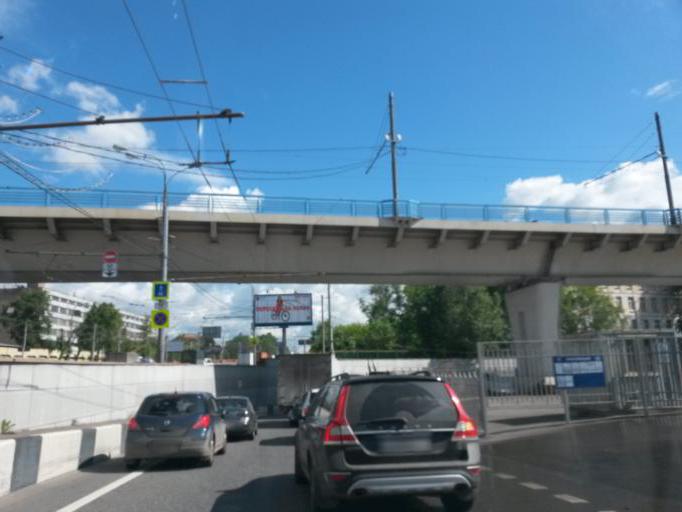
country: RU
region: Moscow
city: Nagornyy
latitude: 55.6632
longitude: 37.6202
